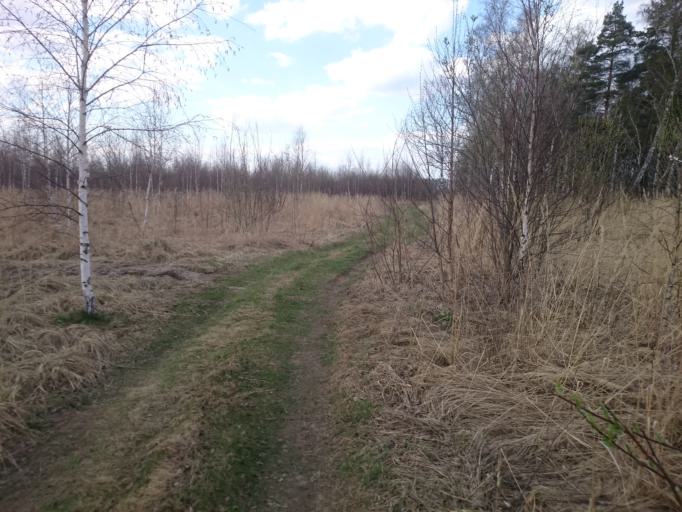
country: RU
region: Moskovskaya
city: Klin
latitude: 56.3977
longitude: 36.6817
